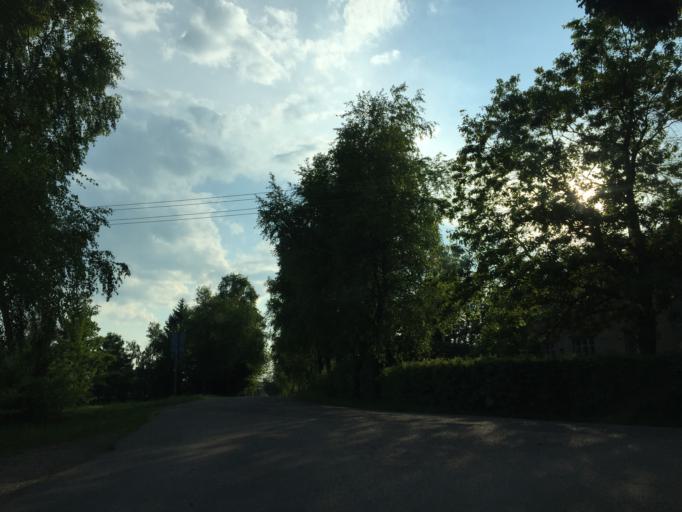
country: LT
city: Plateliai
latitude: 56.0481
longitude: 21.8253
